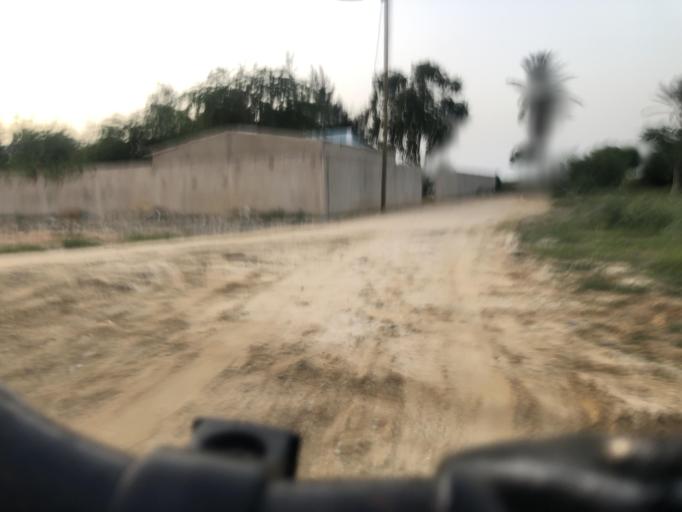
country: SN
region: Saint-Louis
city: Saint-Louis
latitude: 16.0724
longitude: -16.4340
